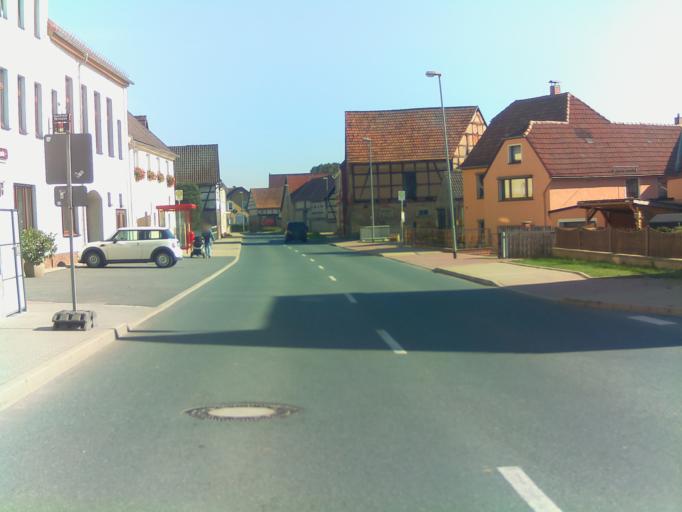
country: DE
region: Thuringia
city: Saara
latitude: 50.8572
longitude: 11.9777
